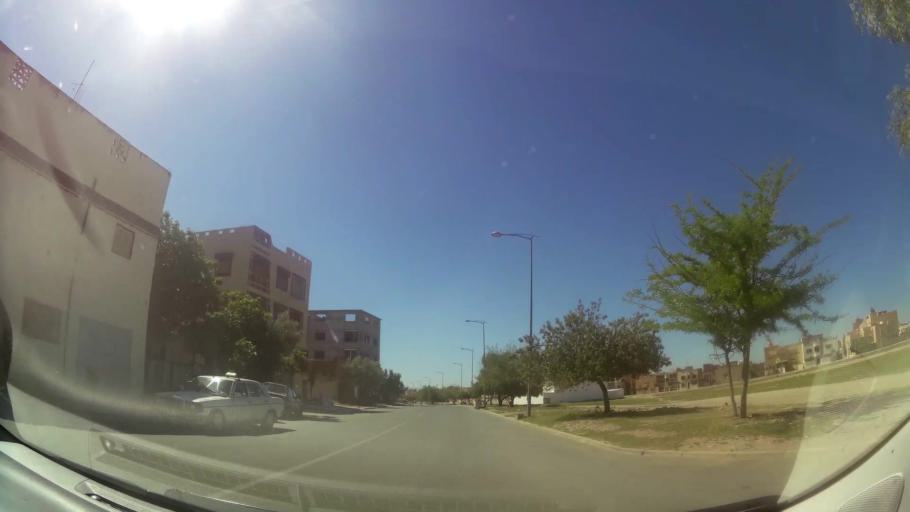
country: MA
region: Oriental
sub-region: Oujda-Angad
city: Oujda
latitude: 34.6658
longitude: -1.8693
